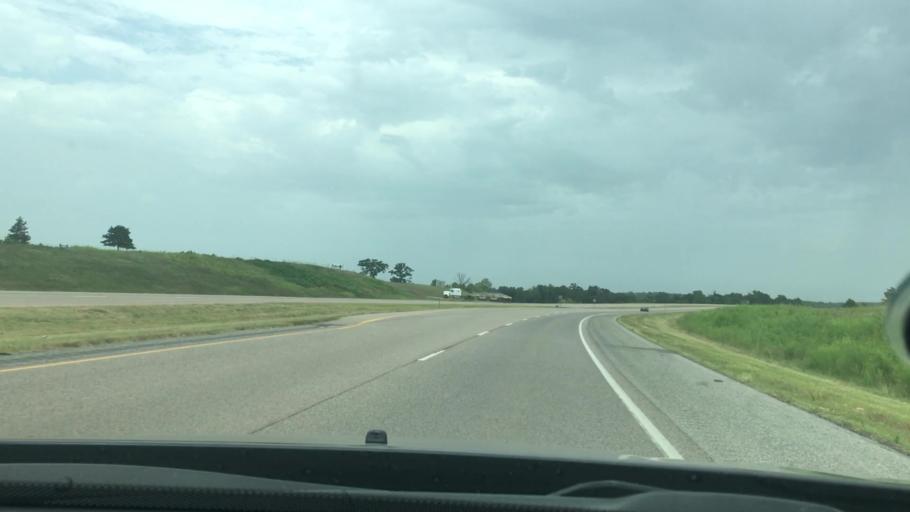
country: US
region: Oklahoma
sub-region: Pontotoc County
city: Byng
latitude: 34.8265
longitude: -96.6938
